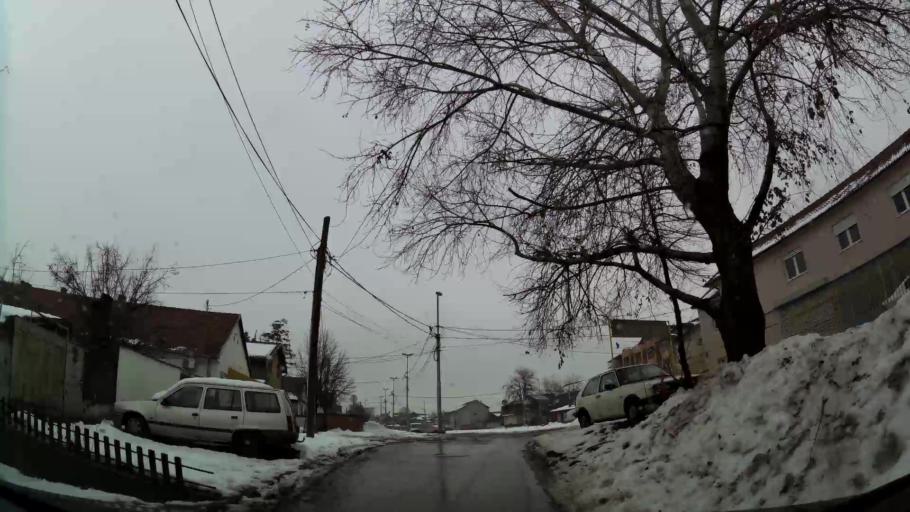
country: RS
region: Central Serbia
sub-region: Belgrade
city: Zemun
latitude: 44.8478
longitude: 20.3791
